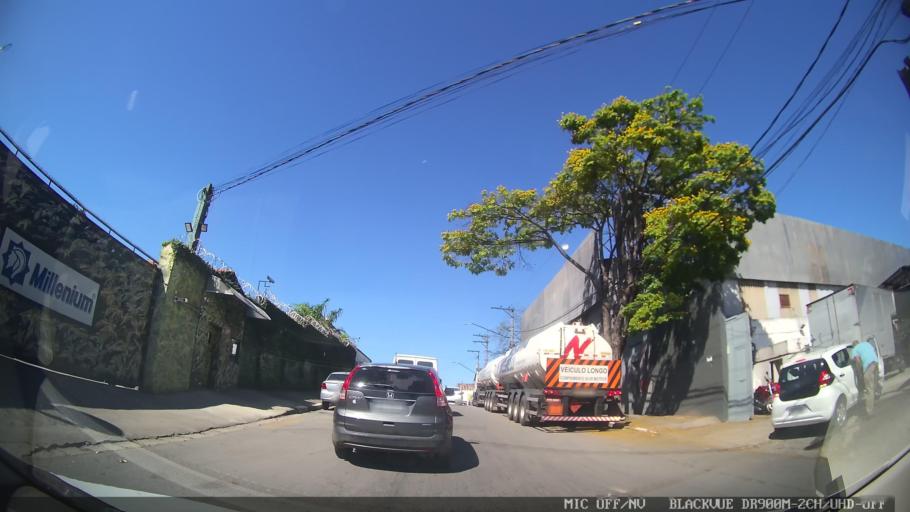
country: BR
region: Sao Paulo
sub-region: Osasco
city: Osasco
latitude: -23.5208
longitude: -46.7837
